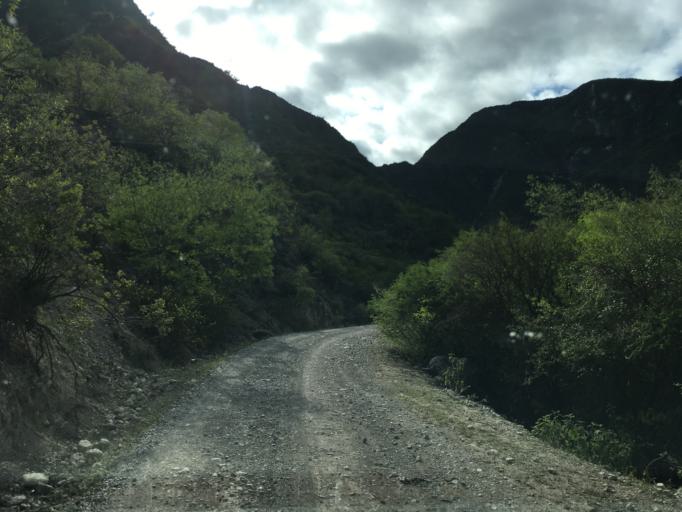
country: MX
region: Hidalgo
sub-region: Metztitlan
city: Fontezuelas
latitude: 20.6366
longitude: -98.9326
